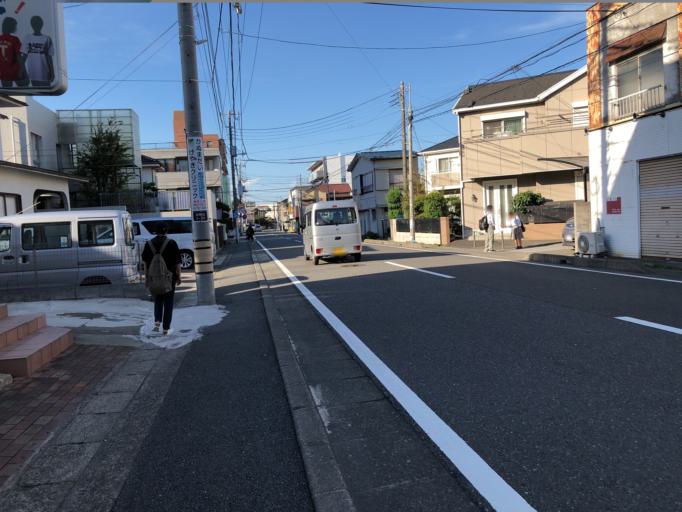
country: JP
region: Tokyo
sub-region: Machida-shi
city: Machida
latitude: 35.5708
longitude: 139.3958
